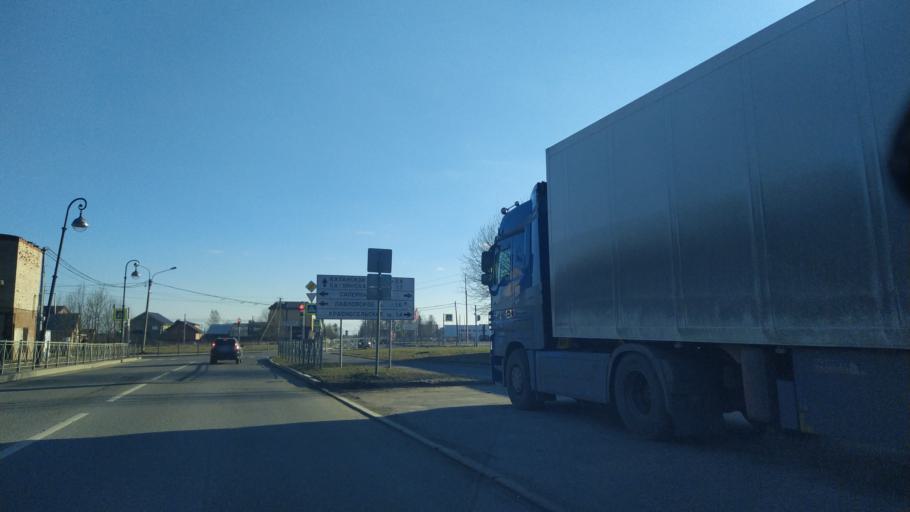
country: RU
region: St.-Petersburg
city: Pushkin
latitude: 59.7014
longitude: 30.3941
